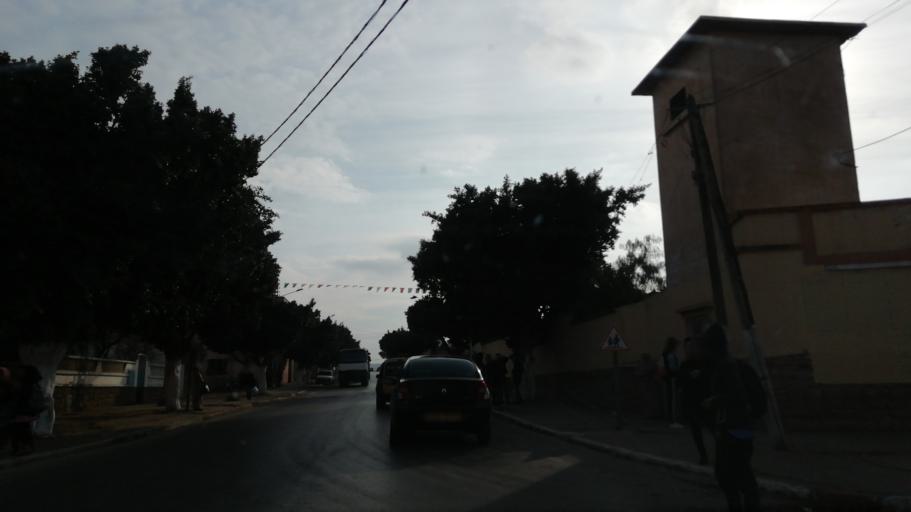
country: DZ
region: Mostaganem
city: Mostaganem
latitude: 35.8571
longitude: 0.0722
